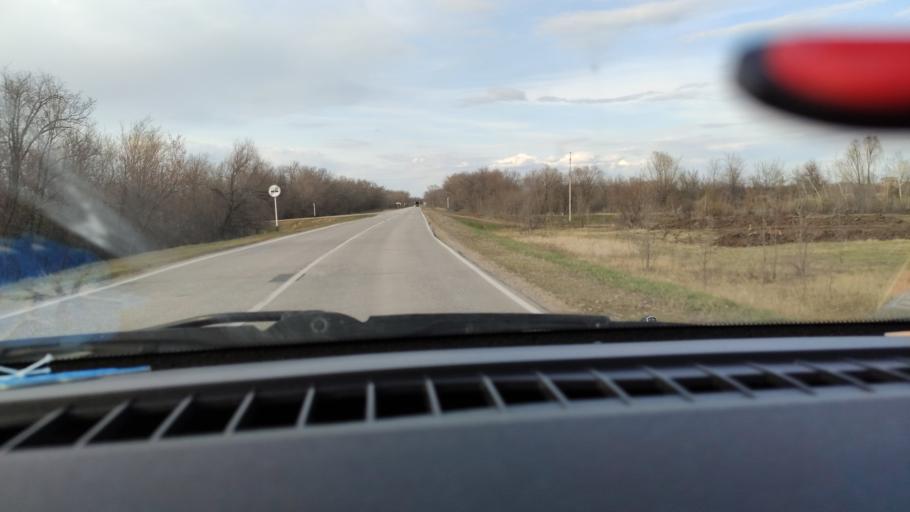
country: RU
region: Saratov
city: Privolzhskiy
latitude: 51.2777
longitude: 45.9514
